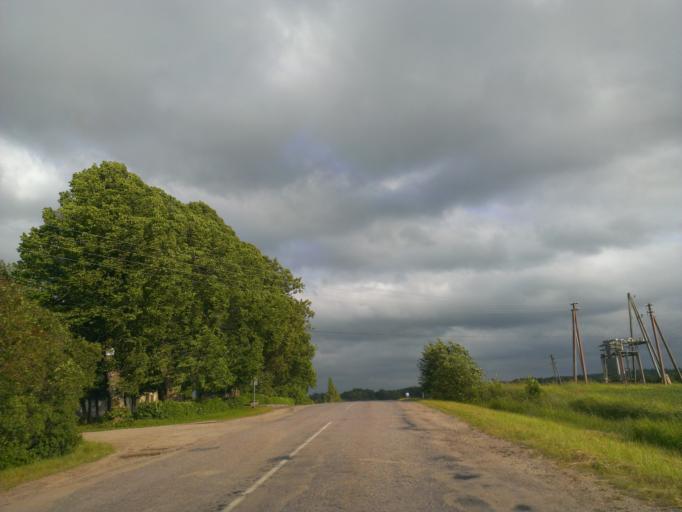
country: LV
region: Aizpute
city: Aizpute
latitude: 56.7160
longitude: 21.7605
